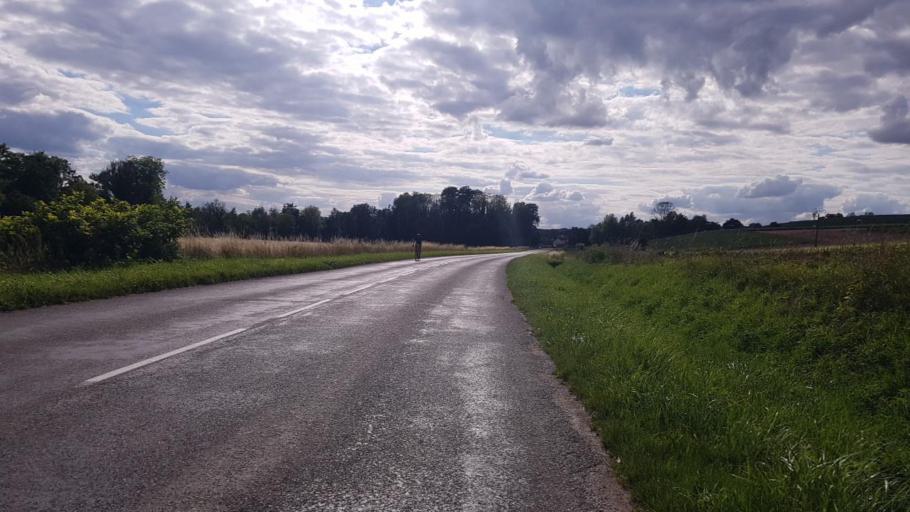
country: FR
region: Picardie
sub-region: Departement de l'Aisne
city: Brasles
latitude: 49.0463
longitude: 3.4411
